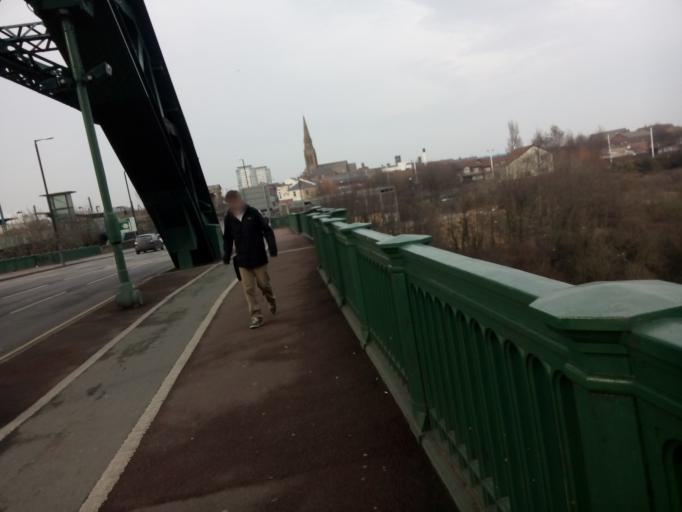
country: GB
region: England
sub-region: Sunderland
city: Sunderland
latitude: 54.9100
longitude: -1.3828
